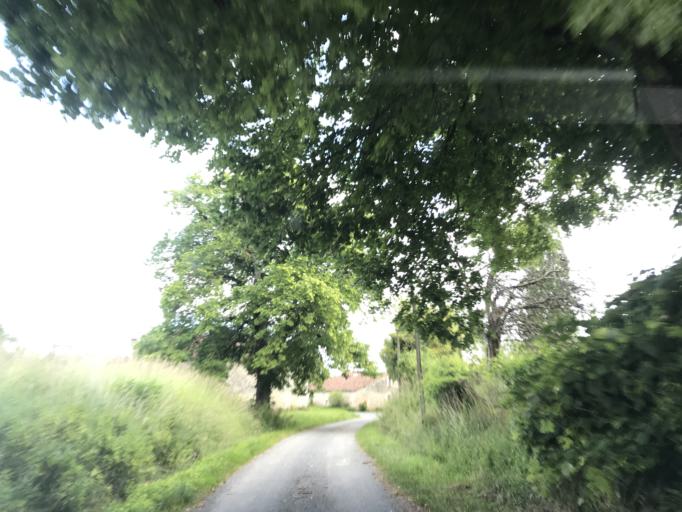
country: FR
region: Aquitaine
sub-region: Departement de la Dordogne
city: Saint-Aulaye
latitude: 45.2607
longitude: 0.1311
